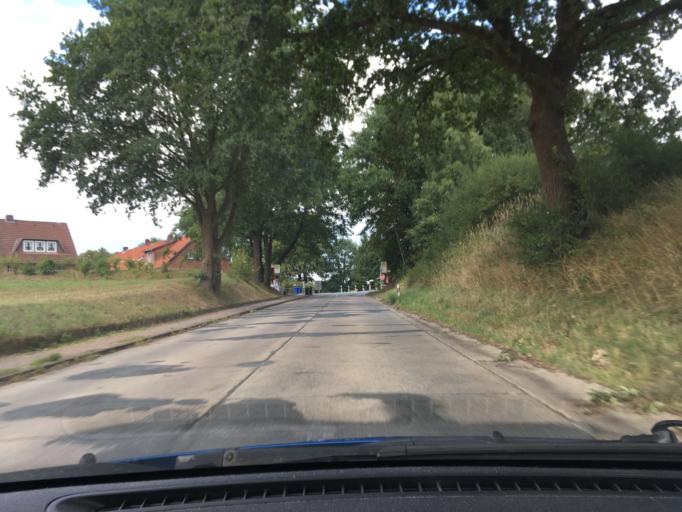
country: DE
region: Lower Saxony
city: Egestorf
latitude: 53.2051
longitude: 10.0306
